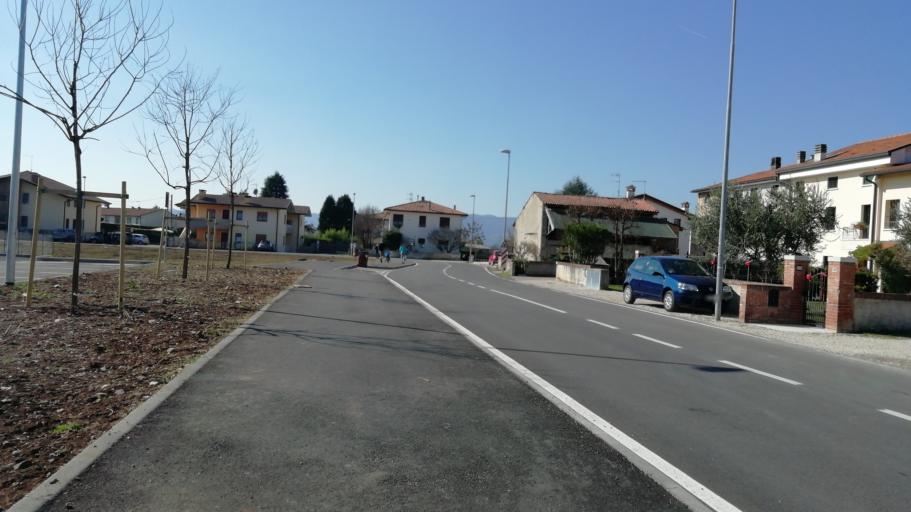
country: IT
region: Veneto
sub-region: Provincia di Vicenza
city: Thiene
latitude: 45.7043
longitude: 11.4627
